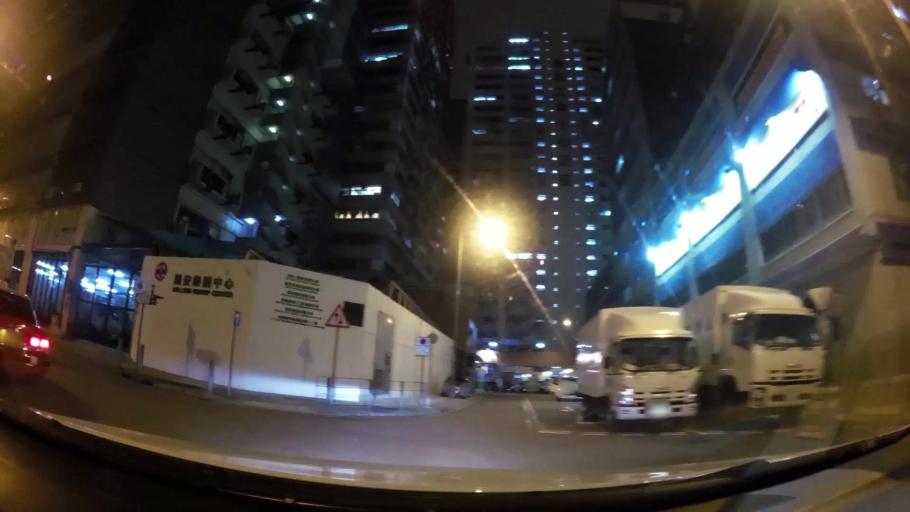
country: HK
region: Tsuen Wan
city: Tsuen Wan
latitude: 22.3593
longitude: 114.1315
